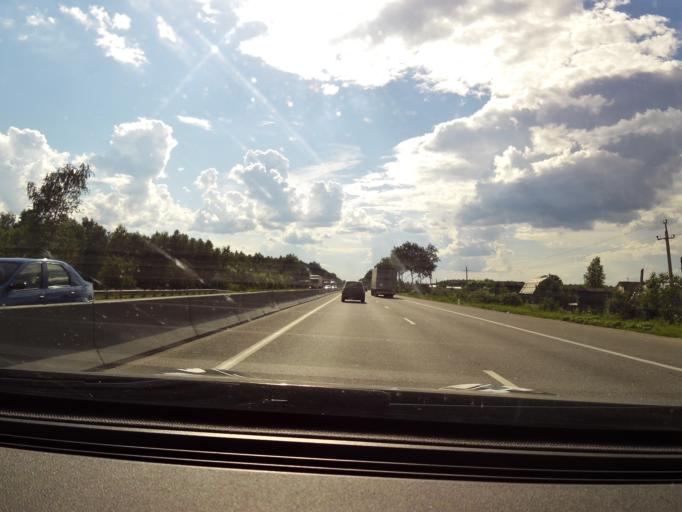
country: RU
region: Nizjnij Novgorod
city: Babino
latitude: 56.3055
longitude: 43.6503
